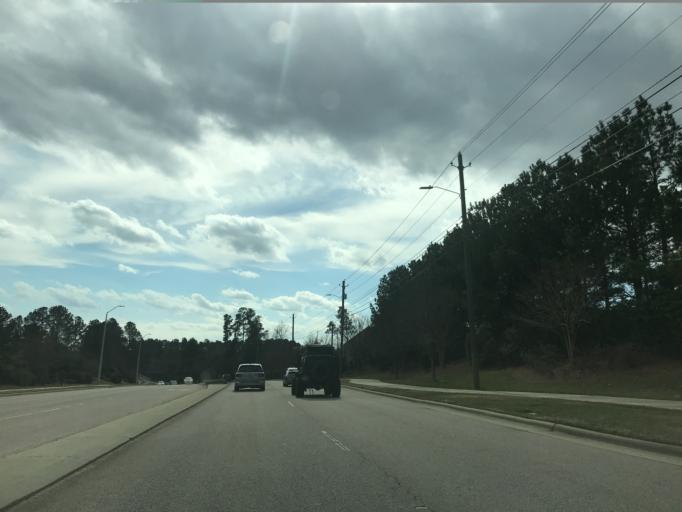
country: US
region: North Carolina
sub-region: Wake County
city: Morrisville
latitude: 35.7996
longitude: -78.8488
